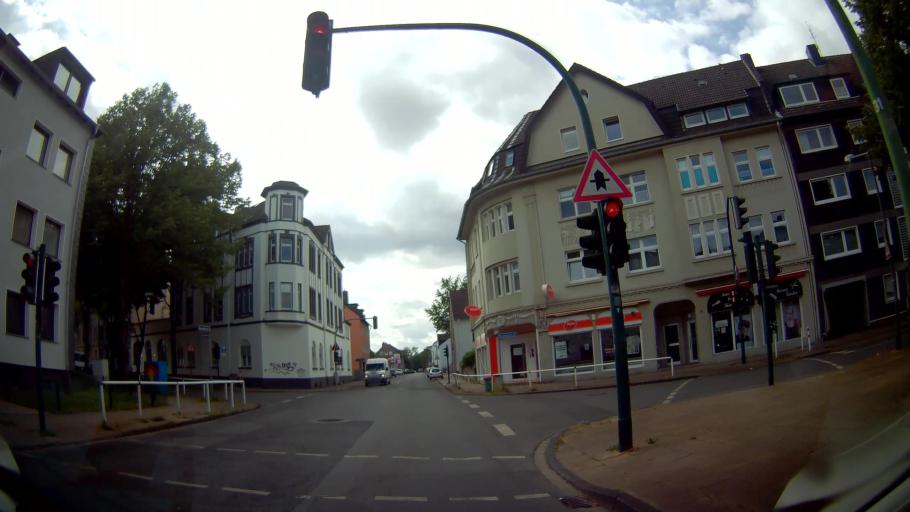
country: DE
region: North Rhine-Westphalia
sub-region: Regierungsbezirk Munster
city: Bottrop
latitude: 51.4919
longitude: 6.9413
